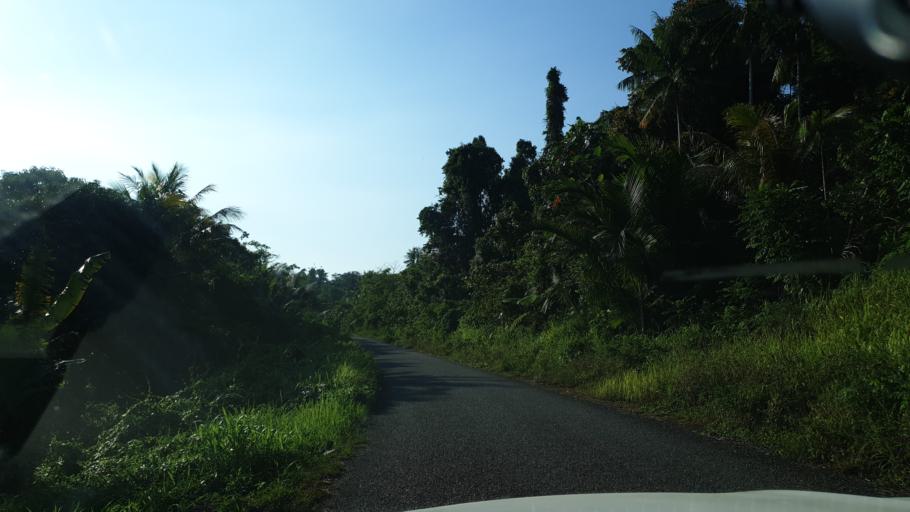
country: PG
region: East Sepik
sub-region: Wewak
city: Wewak
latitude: -3.6925
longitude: 143.6574
